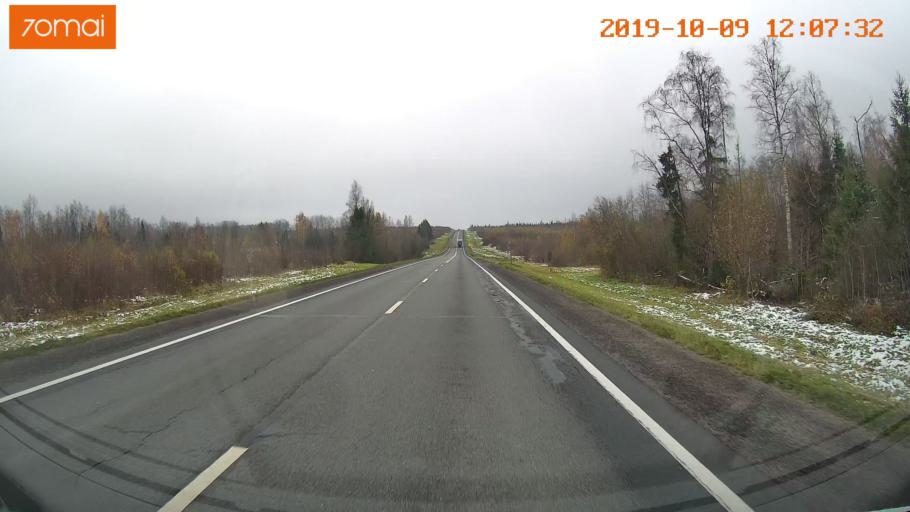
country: RU
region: Jaroslavl
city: Prechistoye
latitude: 58.5980
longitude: 40.3425
